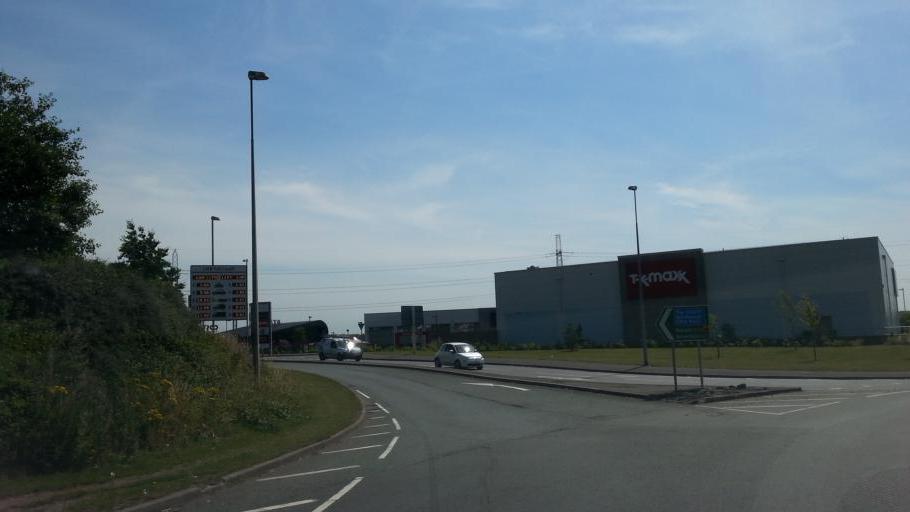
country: GB
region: England
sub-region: Staffordshire
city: Great Wyrley
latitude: 52.6747
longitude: -2.0212
